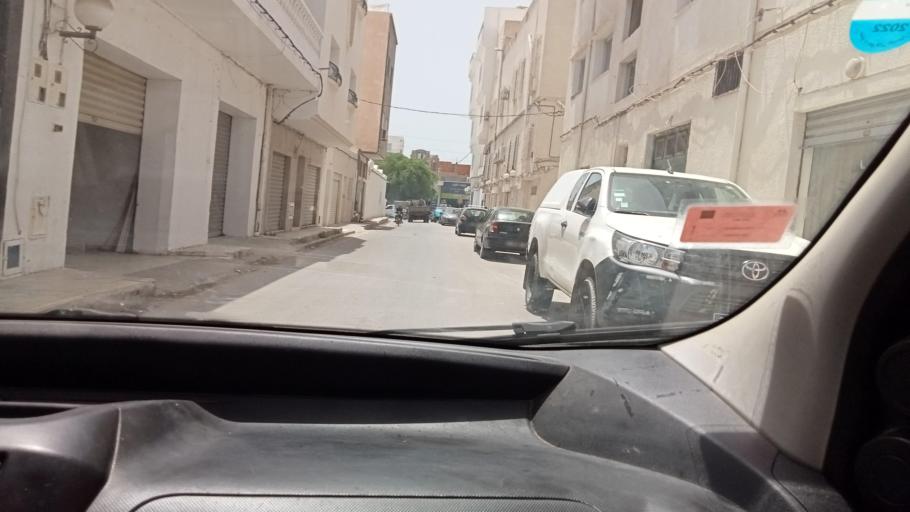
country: TN
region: Nabul
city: Qulaybiyah
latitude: 36.8498
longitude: 11.0879
